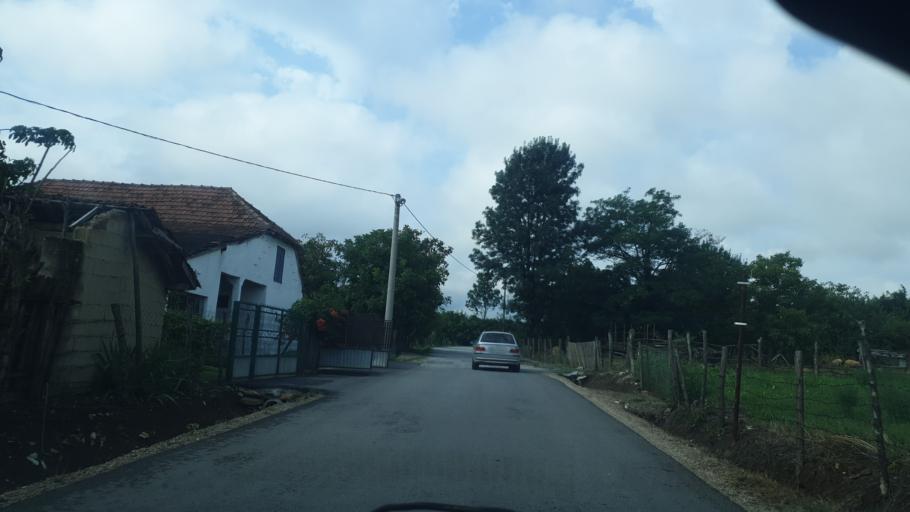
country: RS
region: Central Serbia
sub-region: Sumadijski Okrug
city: Kragujevac
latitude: 44.1083
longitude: 20.8105
